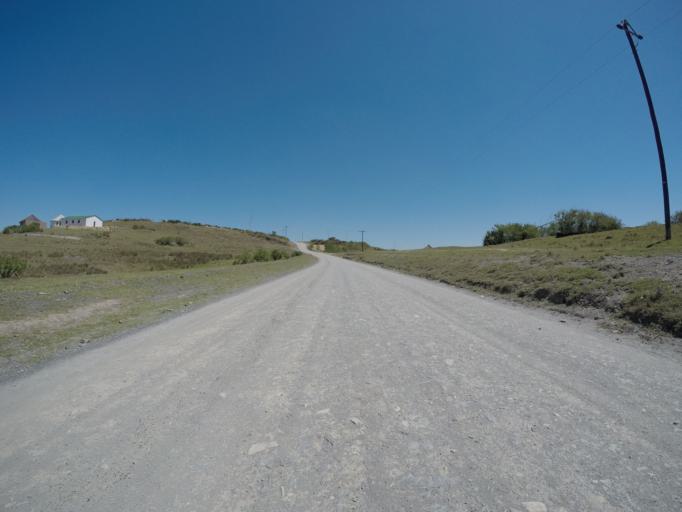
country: ZA
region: Eastern Cape
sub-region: OR Tambo District Municipality
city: Libode
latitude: -31.9831
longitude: 29.0417
